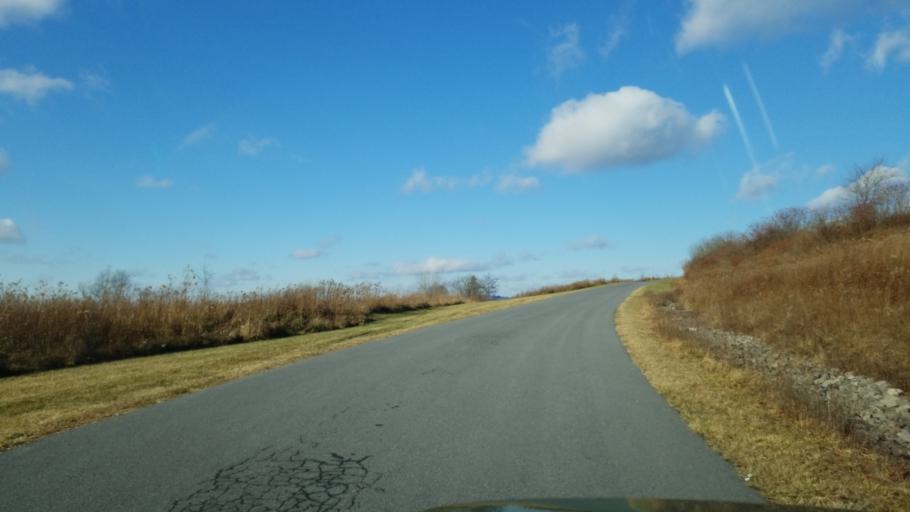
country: US
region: Pennsylvania
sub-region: Clearfield County
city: Clearfield
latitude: 41.0078
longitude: -78.4218
